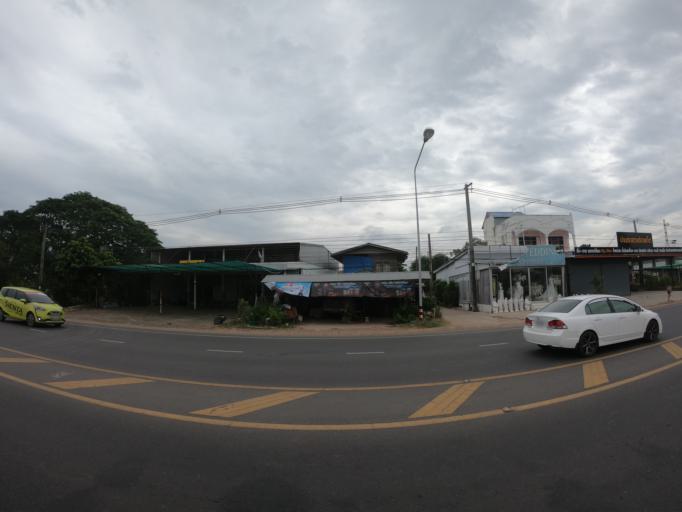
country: TH
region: Roi Et
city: Roi Et
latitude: 16.0748
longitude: 103.6856
